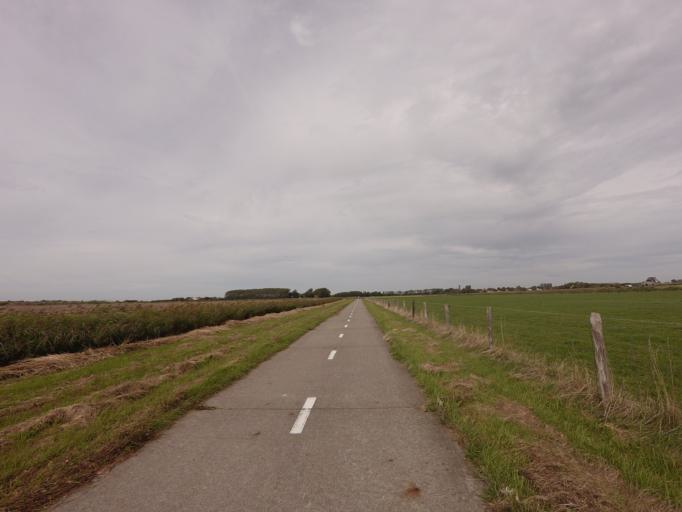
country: NL
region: North Holland
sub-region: Gemeente Texel
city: Den Burg
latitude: 53.0631
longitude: 4.8231
